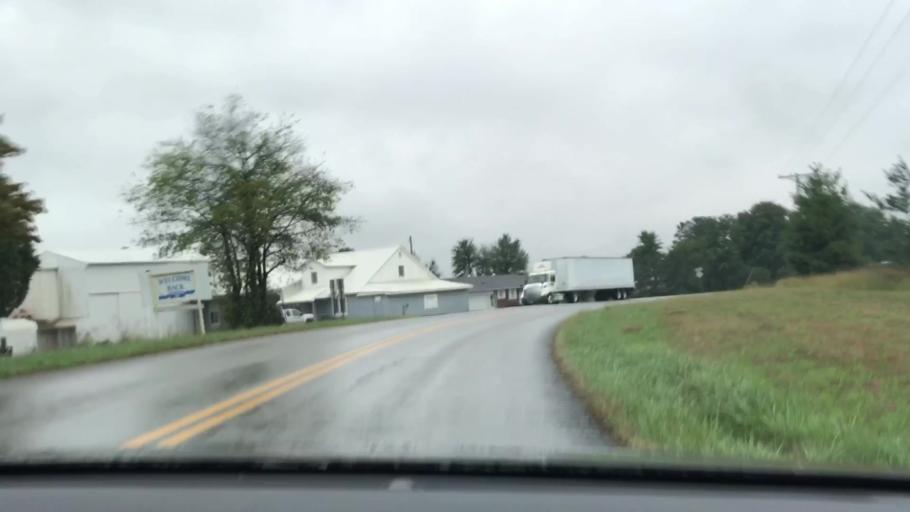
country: US
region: Kentucky
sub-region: McLean County
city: Calhoun
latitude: 37.4058
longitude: -87.2620
